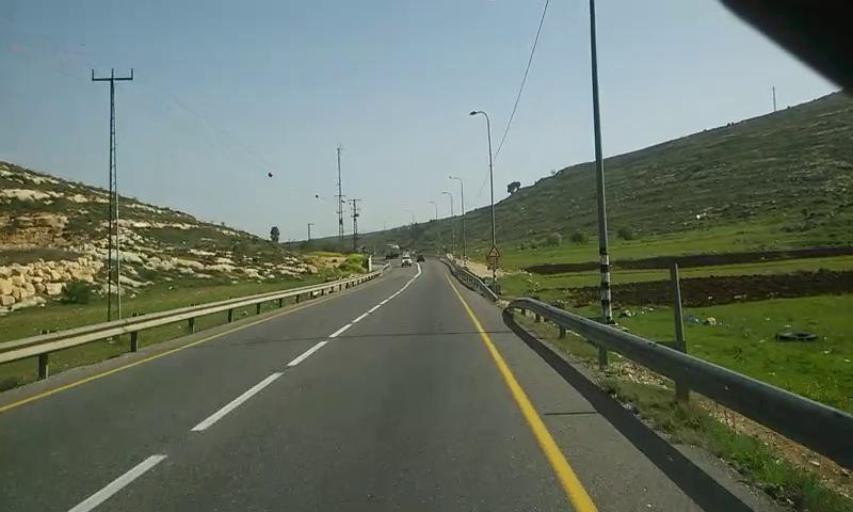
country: PS
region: West Bank
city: Sinjil
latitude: 32.0266
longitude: 35.2737
